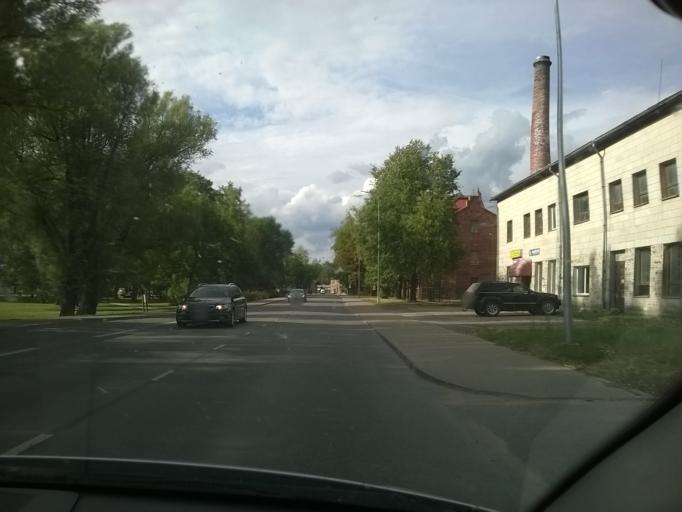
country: EE
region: Vorumaa
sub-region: Voru linn
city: Voru
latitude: 57.8389
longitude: 27.0028
